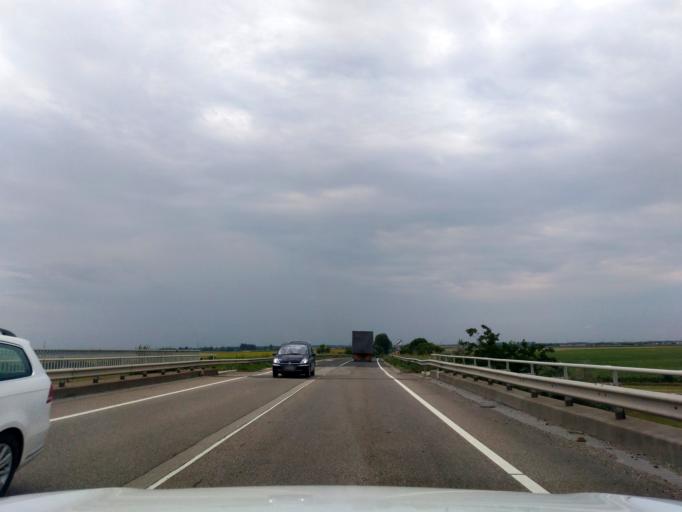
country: HU
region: Jasz-Nagykun-Szolnok
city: Toszeg
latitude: 47.1754
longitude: 20.1021
